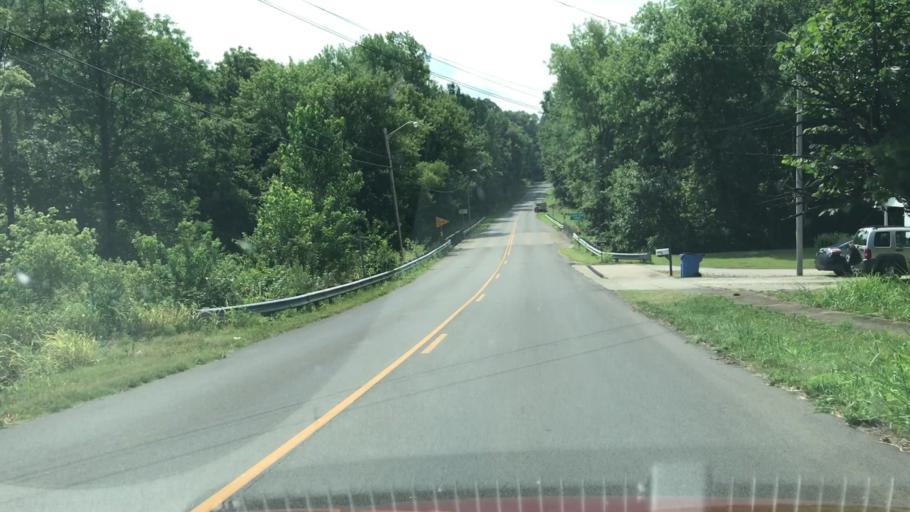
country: US
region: Kentucky
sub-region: Barren County
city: Glasgow
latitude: 36.9885
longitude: -85.9077
